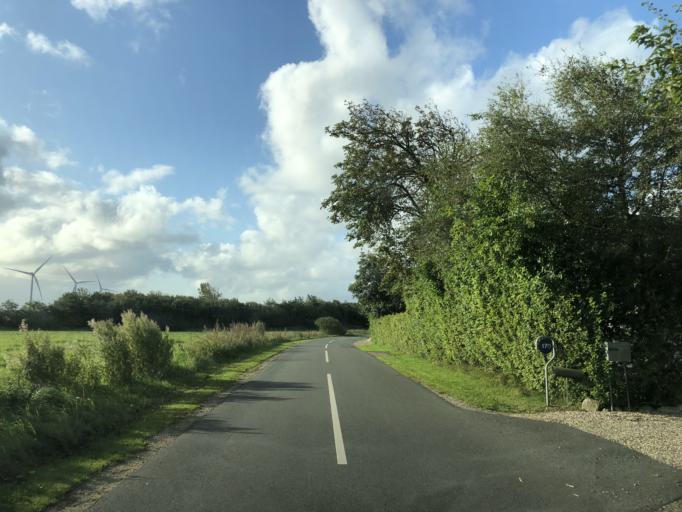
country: DK
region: Central Jutland
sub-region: Holstebro Kommune
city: Ulfborg
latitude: 56.3850
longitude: 8.3477
